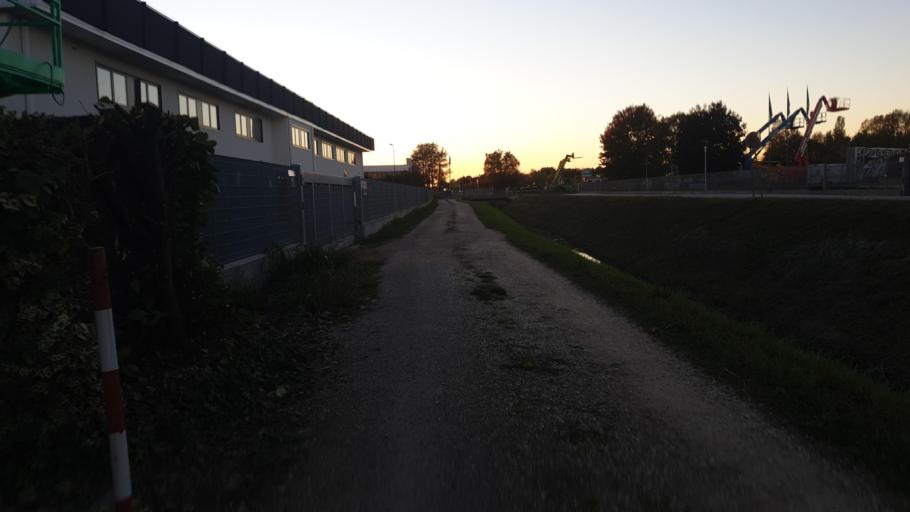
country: IT
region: Veneto
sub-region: Provincia di Venezia
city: Cazzago-Ex Polo
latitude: 45.4434
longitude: 12.0659
